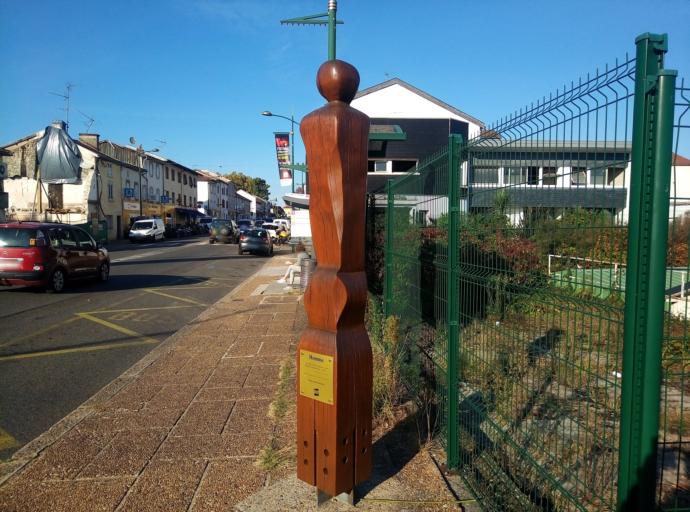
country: FR
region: Aquitaine
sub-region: Departement des Landes
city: Saint-Paul-les-Dax
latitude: 43.7214
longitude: -1.0519
